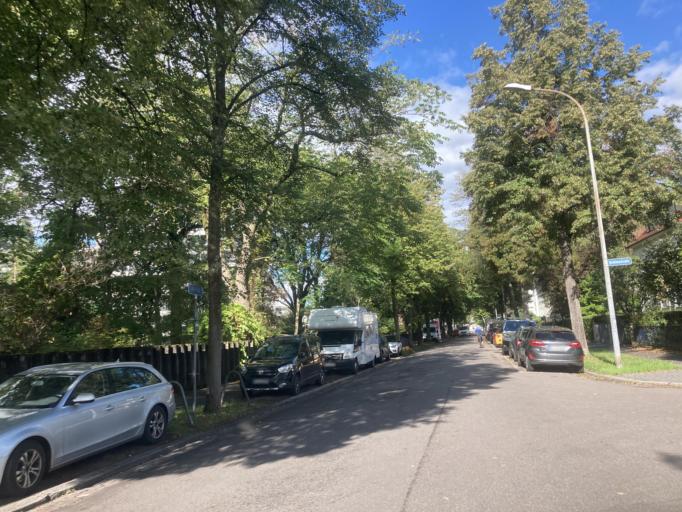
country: DE
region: Baden-Wuerttemberg
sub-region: Freiburg Region
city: Freiburg
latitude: 48.0100
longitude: 7.8597
